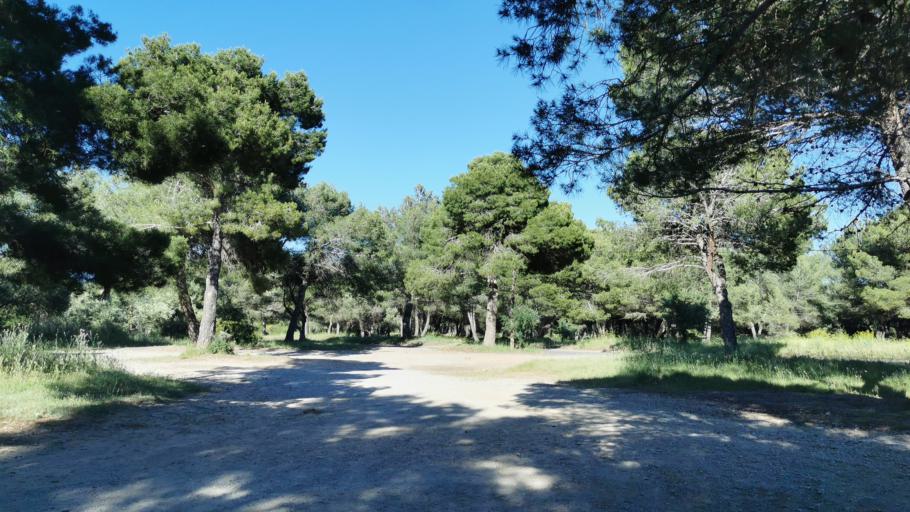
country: FR
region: Languedoc-Roussillon
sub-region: Departement de l'Aude
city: Gruissan
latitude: 43.1307
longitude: 3.1003
